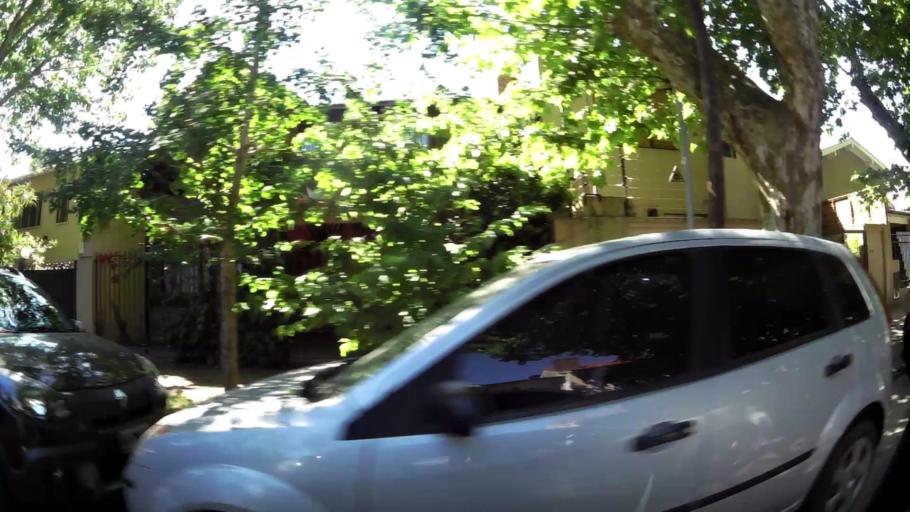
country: AR
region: Buenos Aires
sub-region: Partido de San Isidro
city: San Isidro
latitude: -34.4555
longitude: -58.5278
